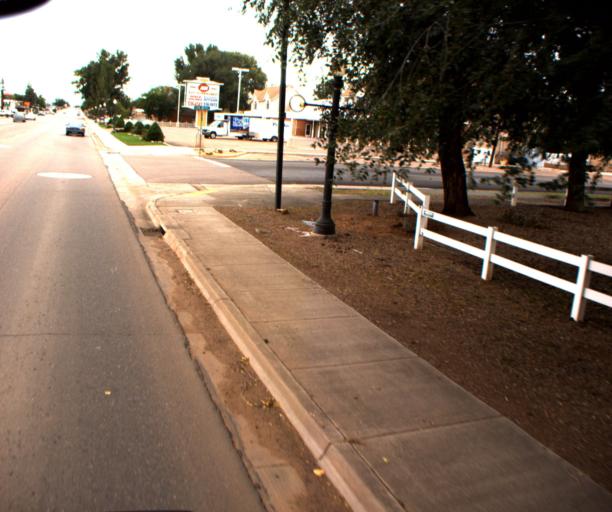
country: US
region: Arizona
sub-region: Navajo County
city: Snowflake
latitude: 34.5123
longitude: -110.0790
